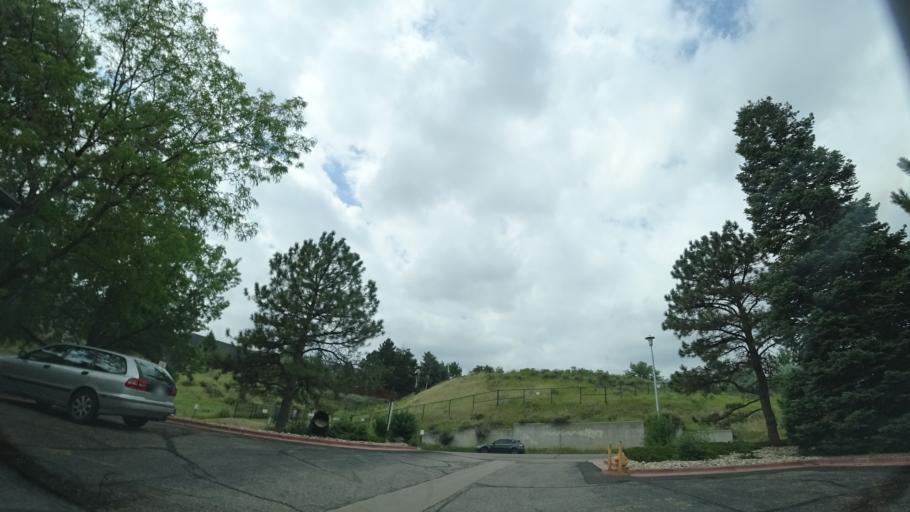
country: US
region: Colorado
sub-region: Jefferson County
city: West Pleasant View
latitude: 39.7132
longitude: -105.1625
